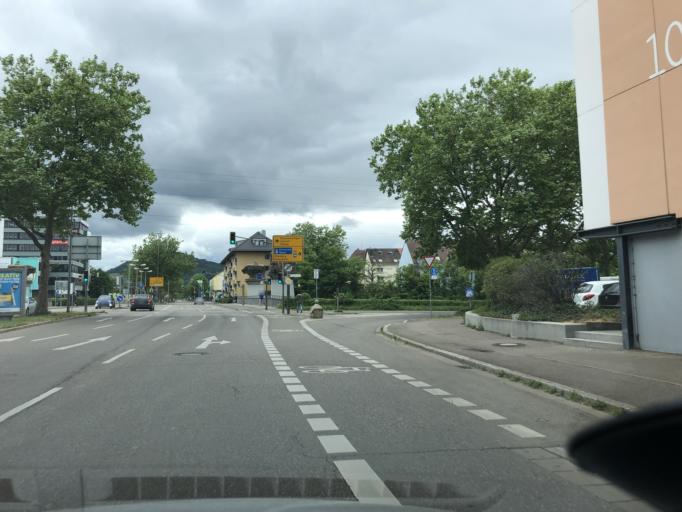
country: DE
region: Baden-Wuerttemberg
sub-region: Freiburg Region
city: Freiburg
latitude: 47.9945
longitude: 7.8333
